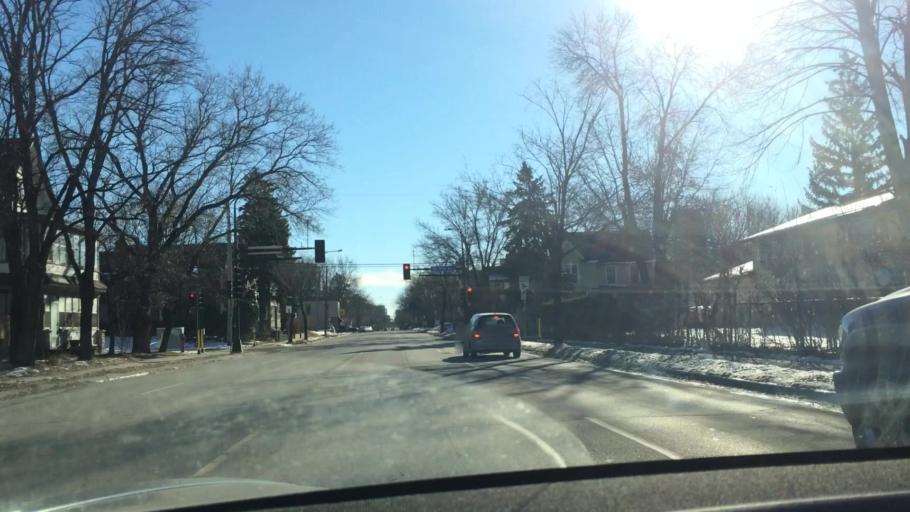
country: US
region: Minnesota
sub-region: Hennepin County
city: Minneapolis
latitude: 44.9971
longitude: -93.2627
